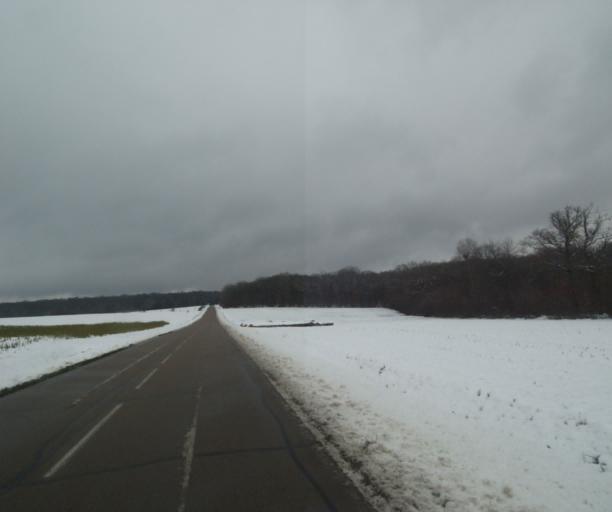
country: FR
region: Champagne-Ardenne
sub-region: Departement de la Haute-Marne
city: Laneuville-a-Remy
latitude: 48.4353
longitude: 4.8557
